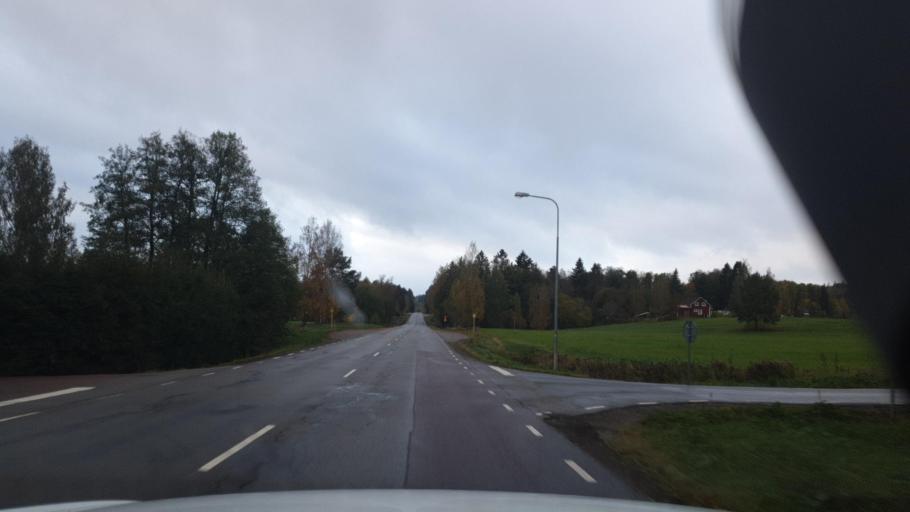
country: SE
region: Vaermland
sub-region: Arvika Kommun
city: Arvika
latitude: 59.6845
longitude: 12.6315
